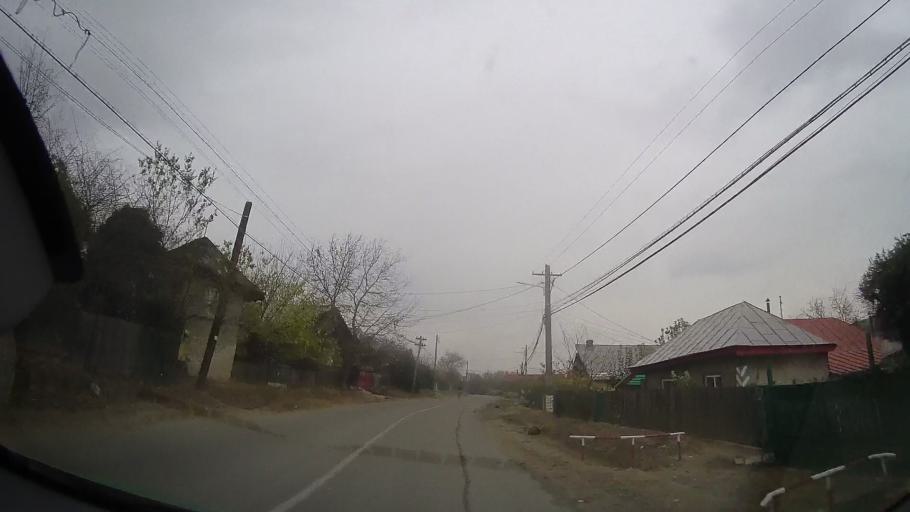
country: RO
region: Prahova
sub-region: Comuna Ceptura
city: Ceptura de Jos
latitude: 45.0260
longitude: 26.3231
